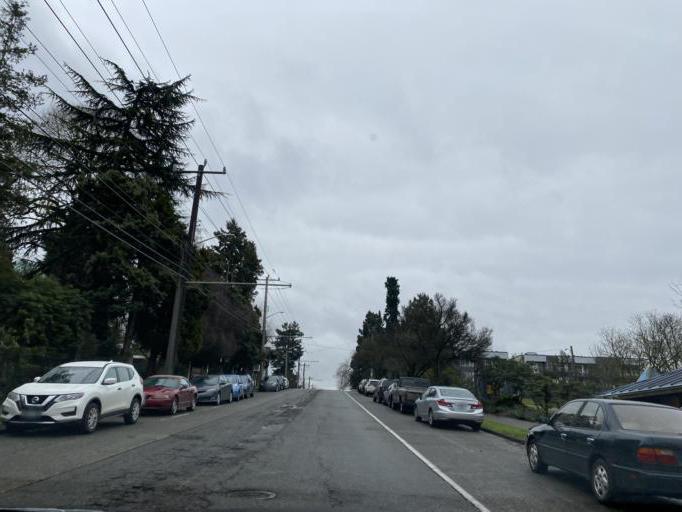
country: US
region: Washington
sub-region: King County
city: Seattle
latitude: 47.5925
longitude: -122.3173
